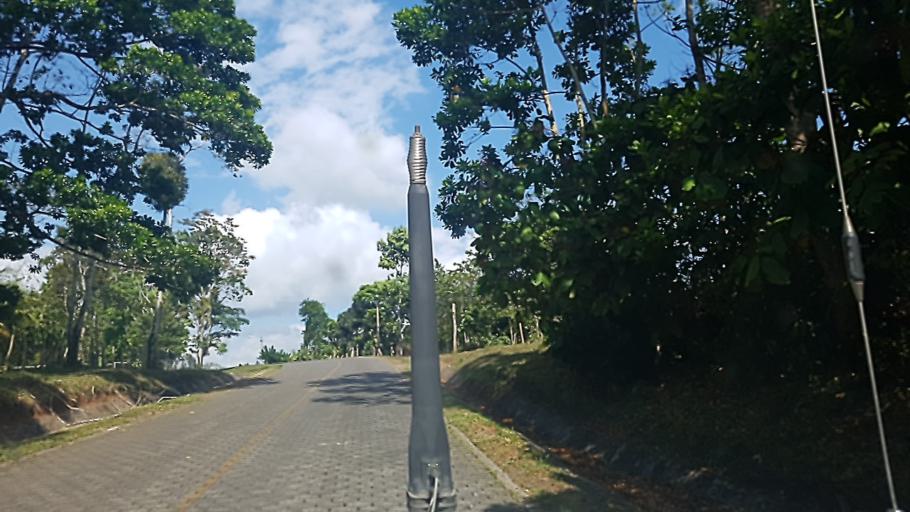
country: NI
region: Atlantico Sur
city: Nueva Guinea
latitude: 11.6972
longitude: -84.3922
